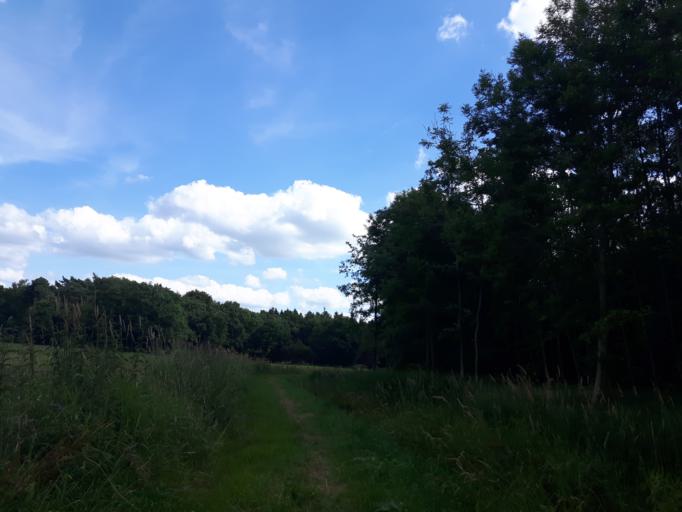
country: NL
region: Overijssel
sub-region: Gemeente Haaksbergen
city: Haaksbergen
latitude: 52.1869
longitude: 6.7715
